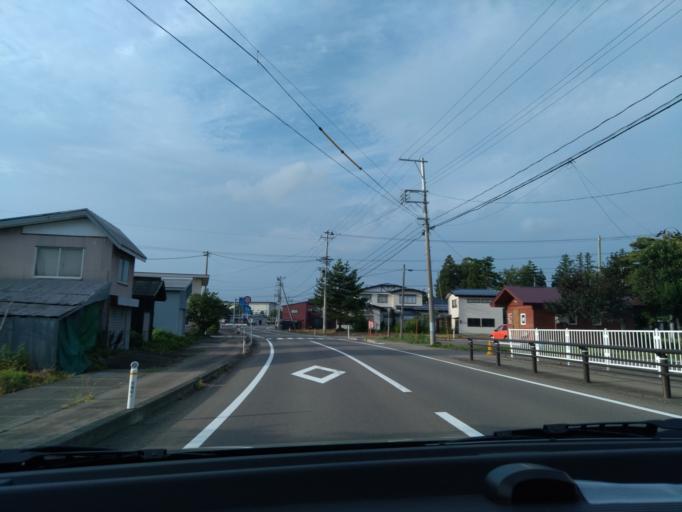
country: JP
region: Akita
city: Yokotemachi
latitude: 39.3839
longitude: 140.5305
